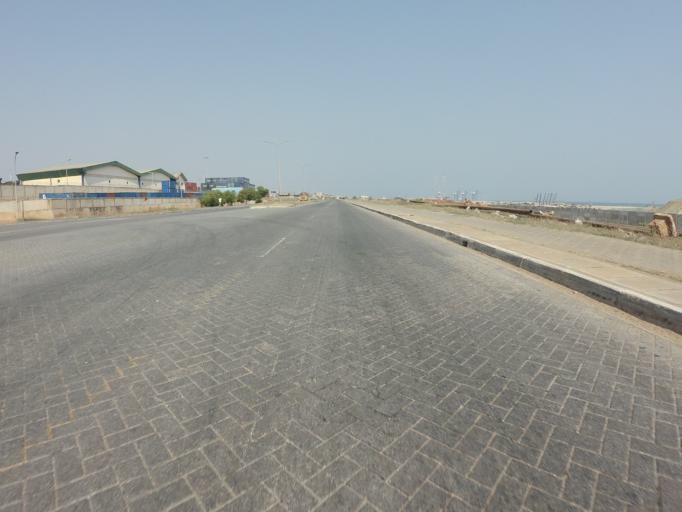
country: GH
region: Greater Accra
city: Tema
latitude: 5.6210
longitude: -0.0130
